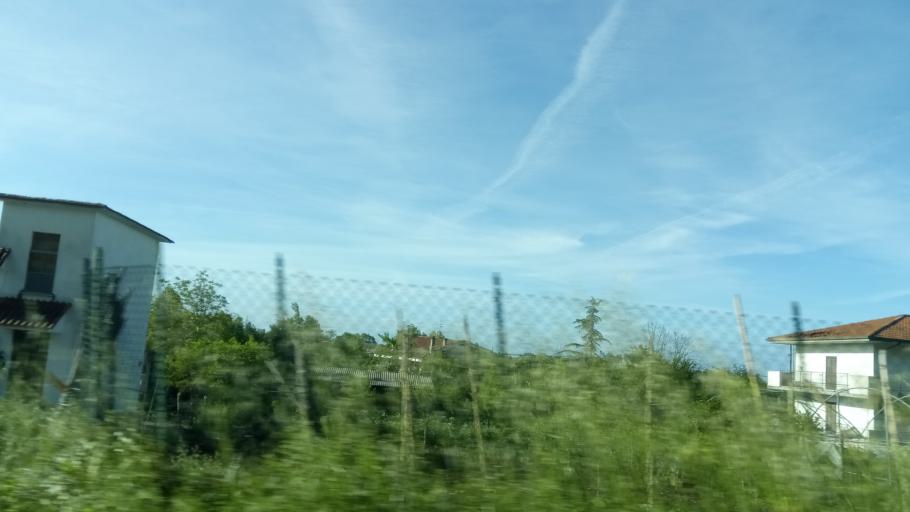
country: IT
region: Latium
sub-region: Provincia di Latina
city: Minturno
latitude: 41.2595
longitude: 13.7690
